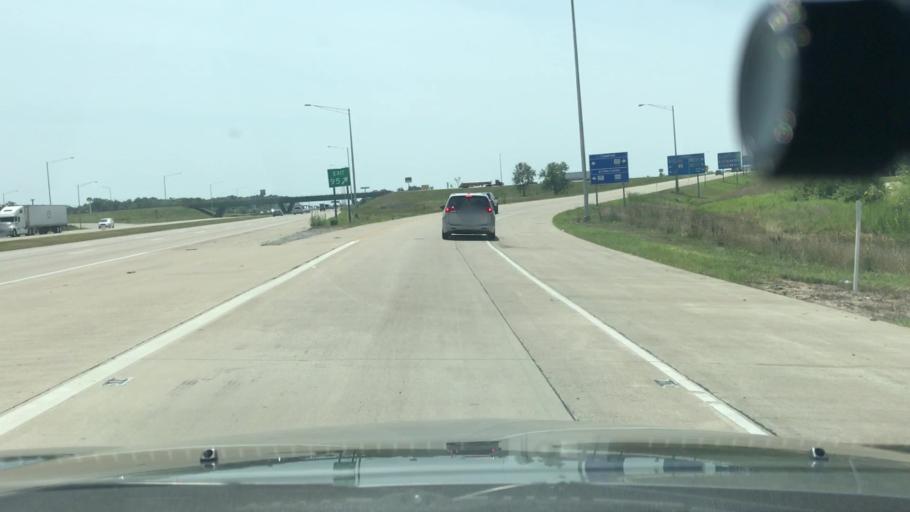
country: US
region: Illinois
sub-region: Jefferson County
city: Mount Vernon
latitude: 38.3164
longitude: -88.9538
